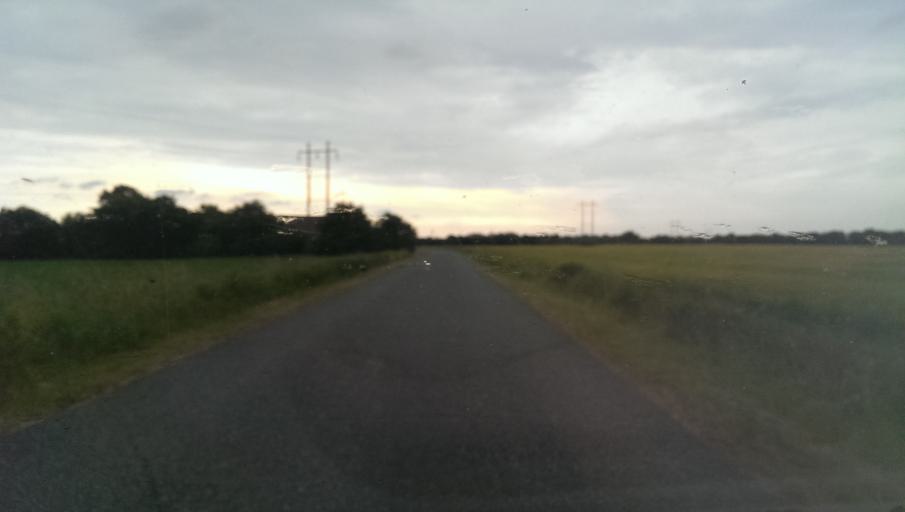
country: DK
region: South Denmark
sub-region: Esbjerg Kommune
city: Bramming
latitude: 55.4353
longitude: 8.7018
